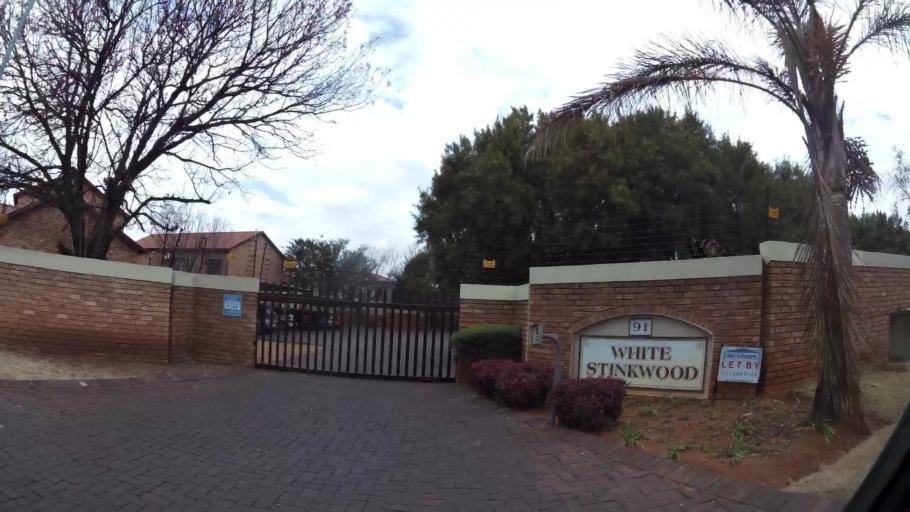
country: ZA
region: Gauteng
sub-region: West Rand District Municipality
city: Muldersdriseloop
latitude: -26.0921
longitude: 27.8720
